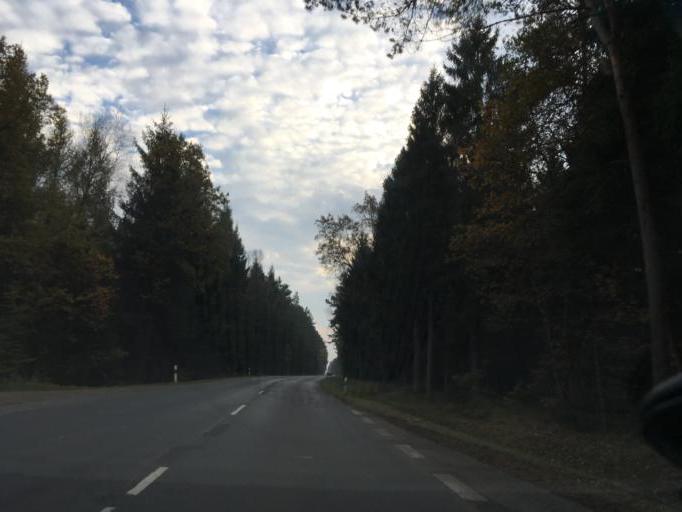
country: DE
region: Lower Saxony
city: Wietzendorf
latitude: 52.9814
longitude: 9.9851
